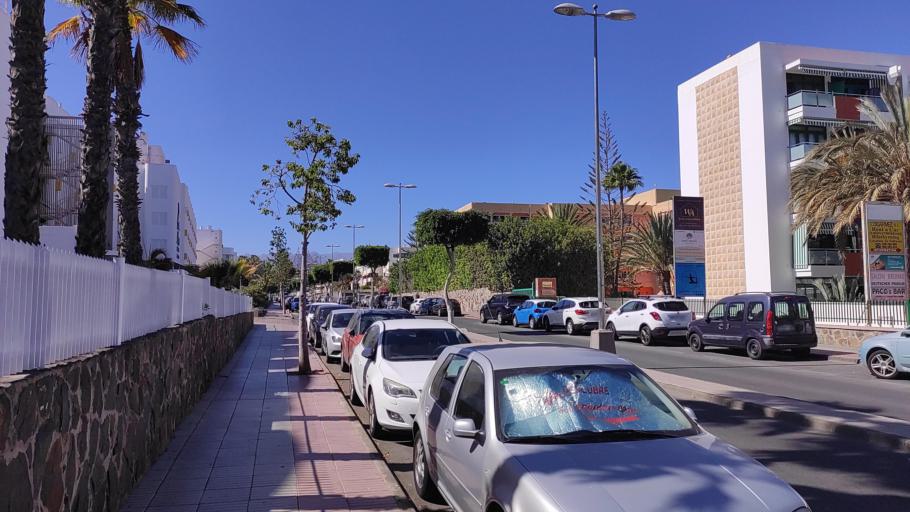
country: ES
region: Canary Islands
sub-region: Provincia de Las Palmas
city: Playa del Ingles
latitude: 27.7483
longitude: -15.5768
